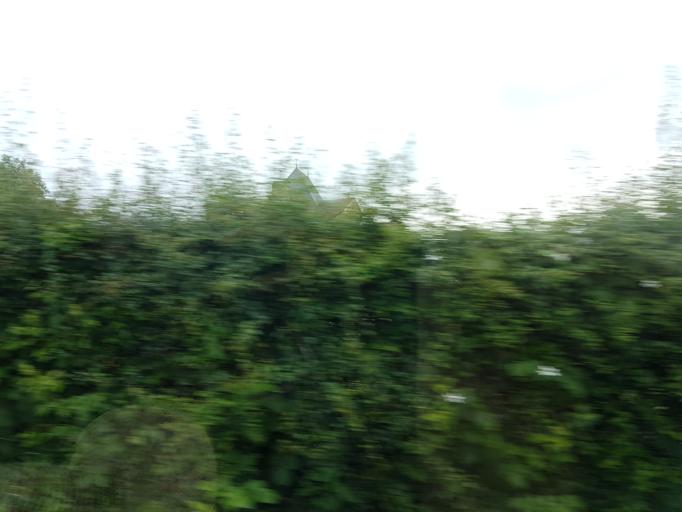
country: FR
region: Bourgogne
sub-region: Departement de la Nievre
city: Corbigny
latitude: 47.2007
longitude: 3.7228
